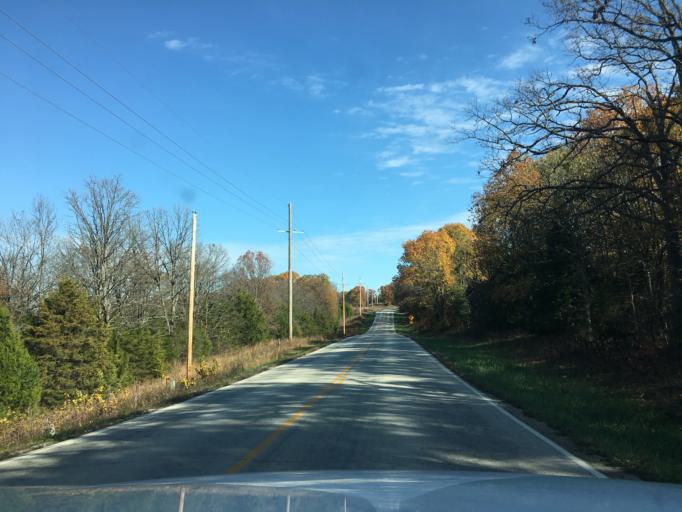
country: US
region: Missouri
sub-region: Maries County
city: Belle
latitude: 38.3367
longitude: -91.7689
